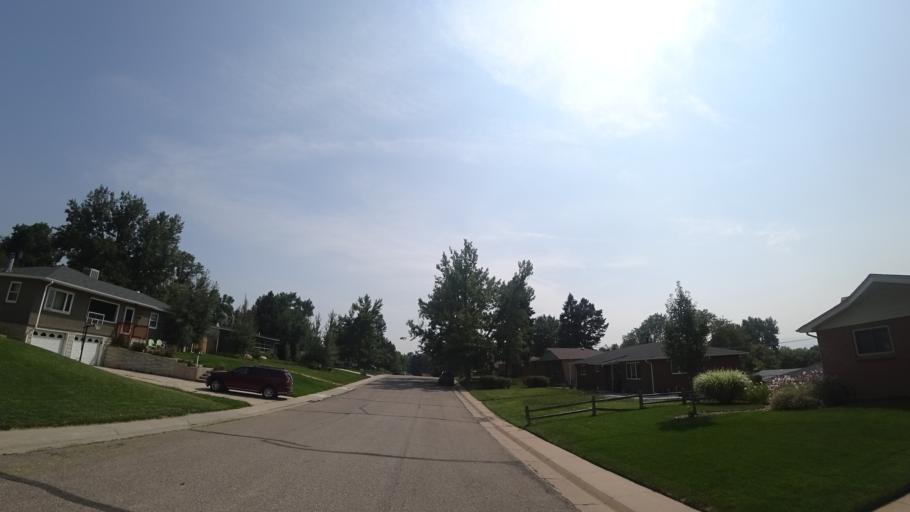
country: US
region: Colorado
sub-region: Arapahoe County
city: Englewood
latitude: 39.6294
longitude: -105.0008
